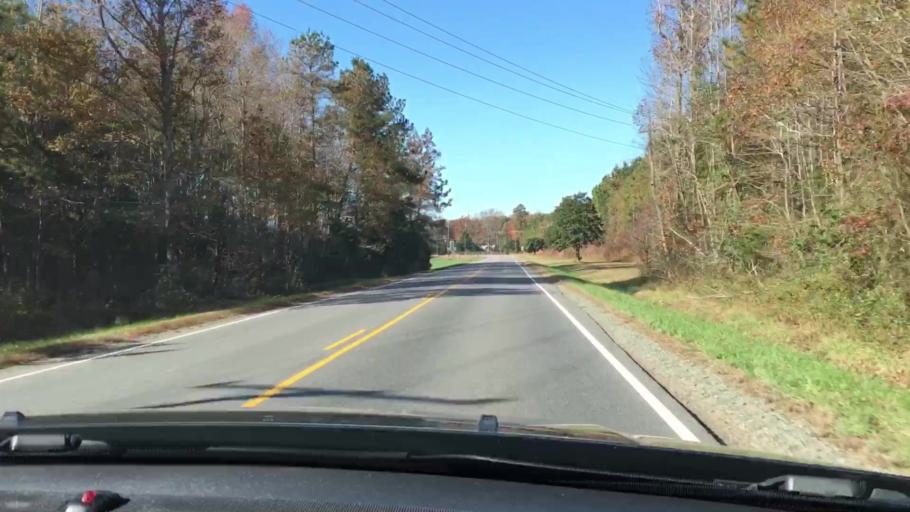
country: US
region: Virginia
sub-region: King William County
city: King William
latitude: 37.6696
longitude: -76.9706
